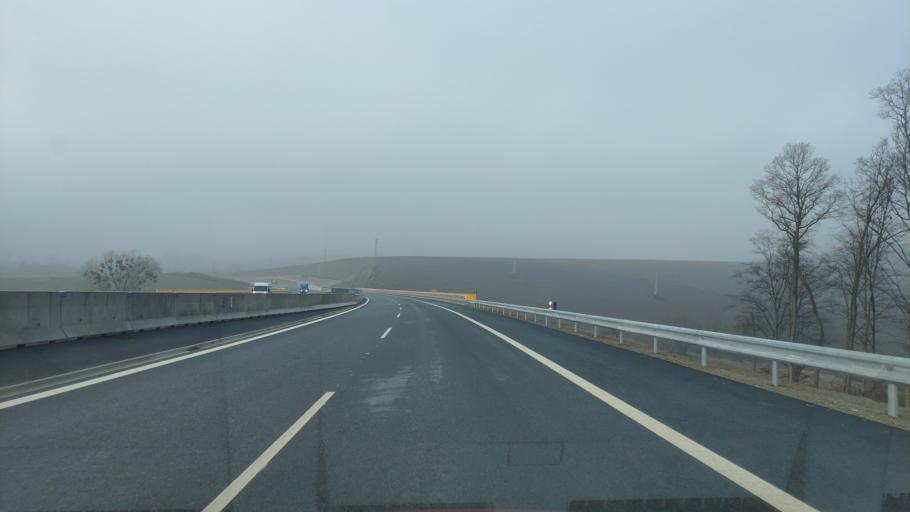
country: SK
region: Kosicky
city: Kosice
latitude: 48.7411
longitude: 21.3792
